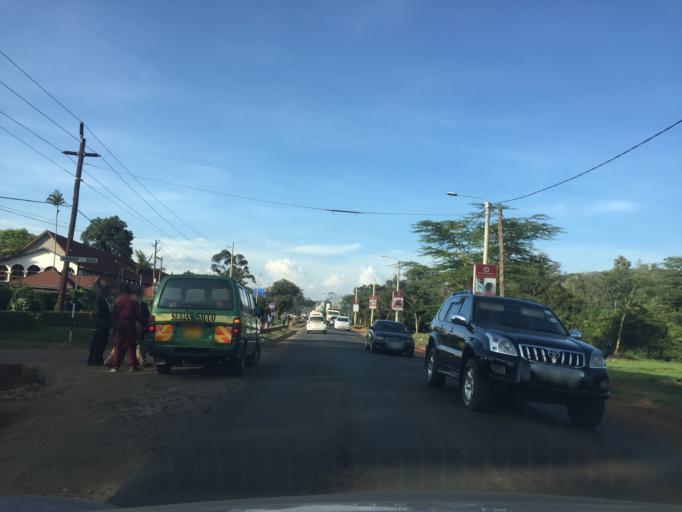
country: KE
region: Nairobi Area
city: Nairobi
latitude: -1.3467
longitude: 36.7654
